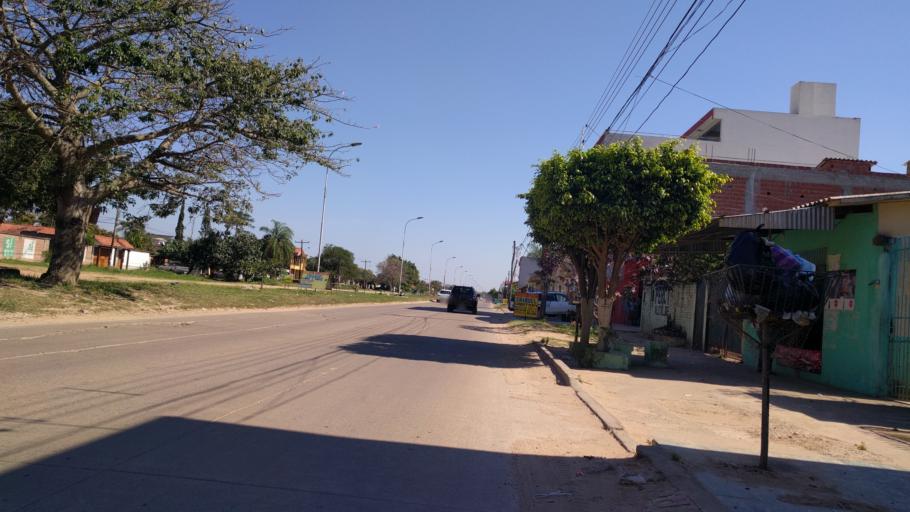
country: BO
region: Santa Cruz
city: Santa Cruz de la Sierra
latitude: -17.8570
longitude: -63.1896
